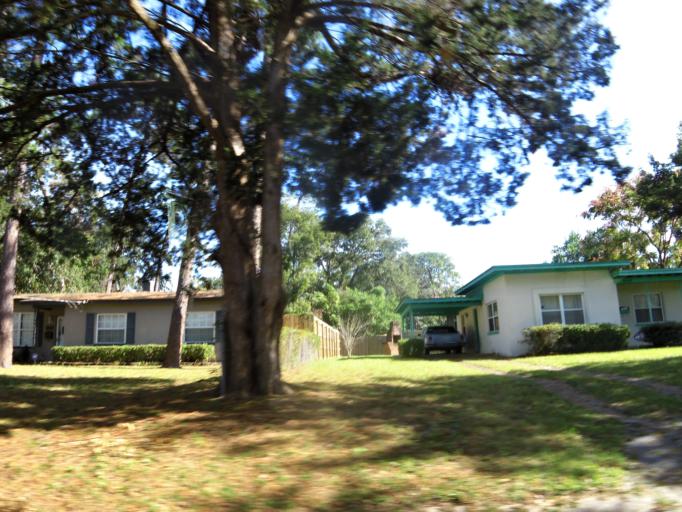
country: US
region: Florida
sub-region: Duval County
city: Jacksonville
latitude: 30.2597
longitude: -81.6342
